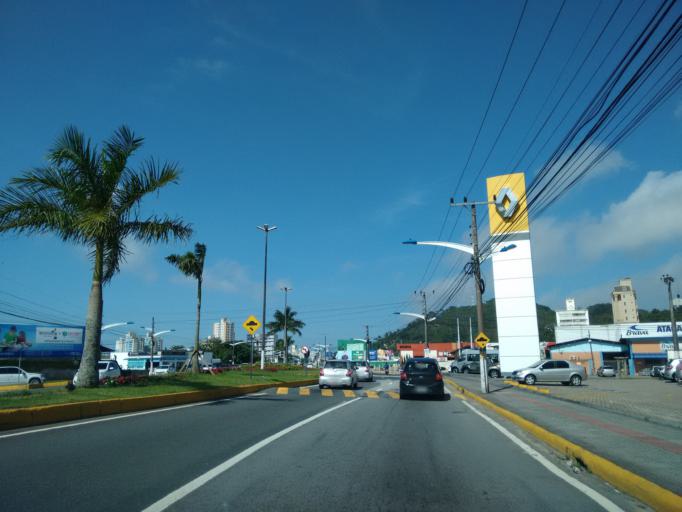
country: BR
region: Santa Catarina
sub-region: Itajai
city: Itajai
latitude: -26.9245
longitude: -48.6775
